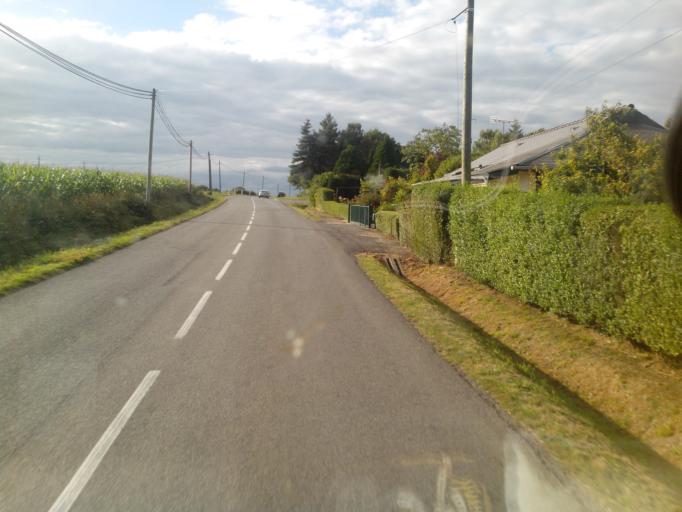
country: FR
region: Brittany
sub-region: Departement d'Ille-et-Vilaine
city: Paimpont
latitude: 48.0379
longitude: -2.1810
